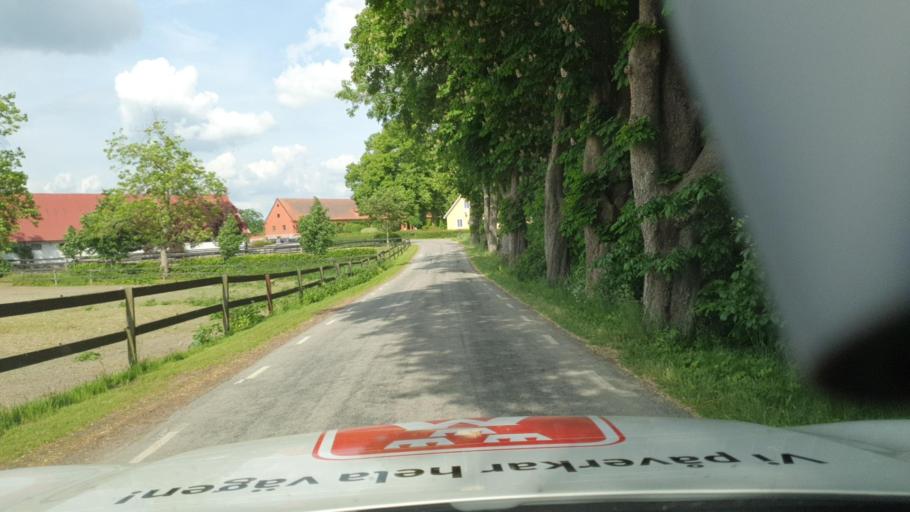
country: SE
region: Skane
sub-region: Skurups Kommun
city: Skurup
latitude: 55.5131
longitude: 13.5035
